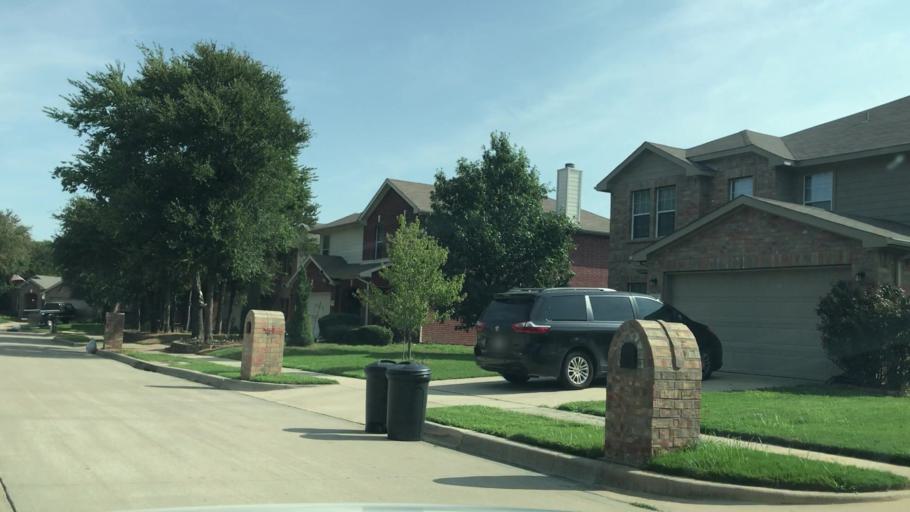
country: US
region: Texas
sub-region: Tarrant County
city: Euless
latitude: 32.8454
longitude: -97.0732
